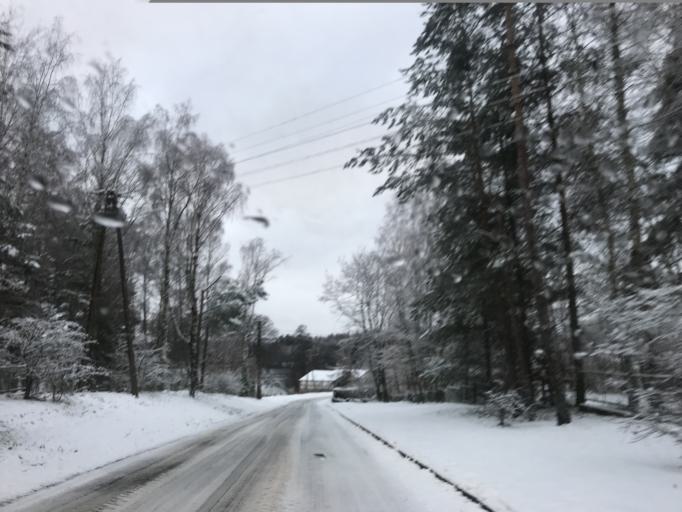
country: PL
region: Pomeranian Voivodeship
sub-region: Powiat bytowski
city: Czarna Dabrowka
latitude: 54.2798
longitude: 17.5928
